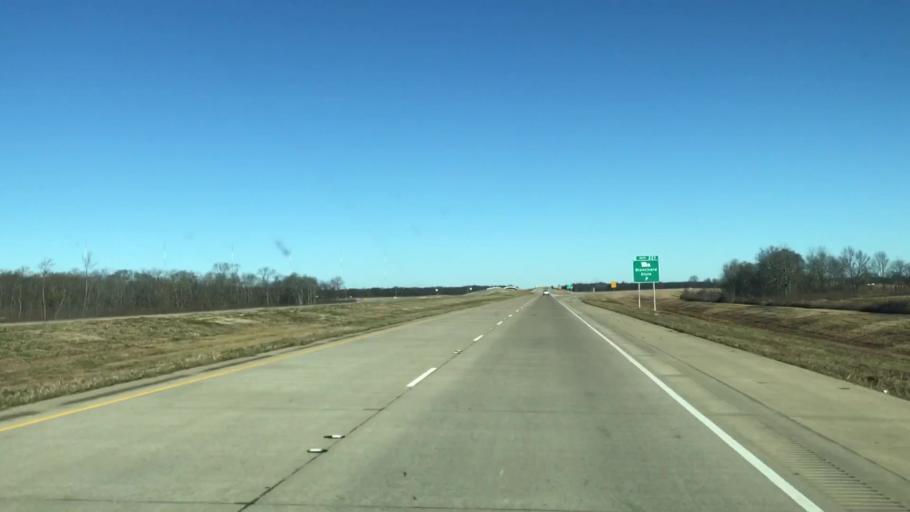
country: US
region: Louisiana
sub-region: Caddo Parish
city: Blanchard
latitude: 32.6683
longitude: -93.8473
